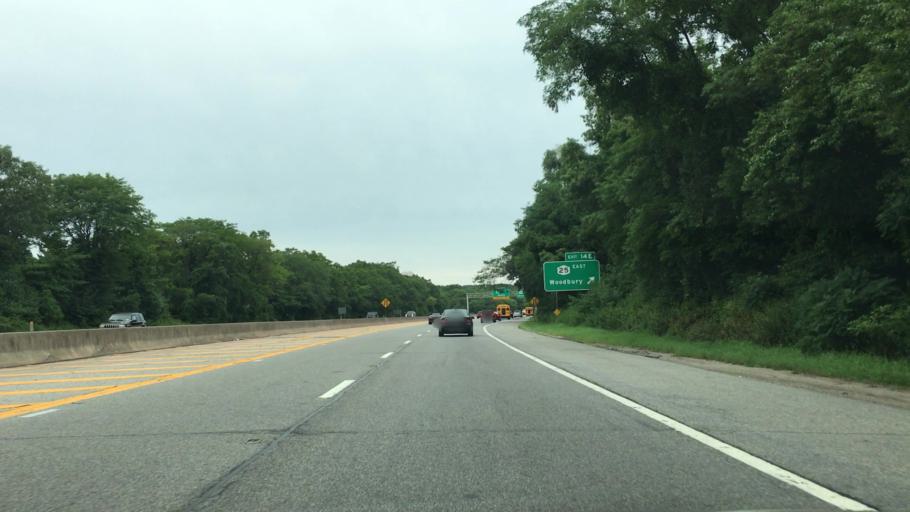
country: US
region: New York
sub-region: Nassau County
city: Syosset
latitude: 40.8062
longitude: -73.4909
